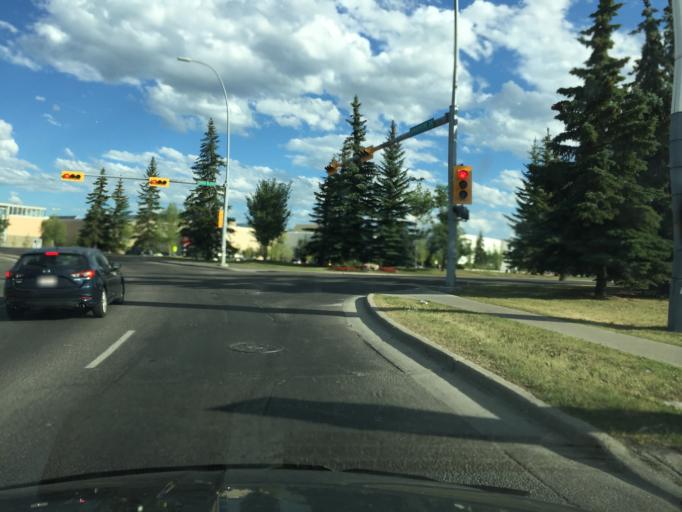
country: CA
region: Alberta
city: Calgary
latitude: 50.9552
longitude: -114.0683
